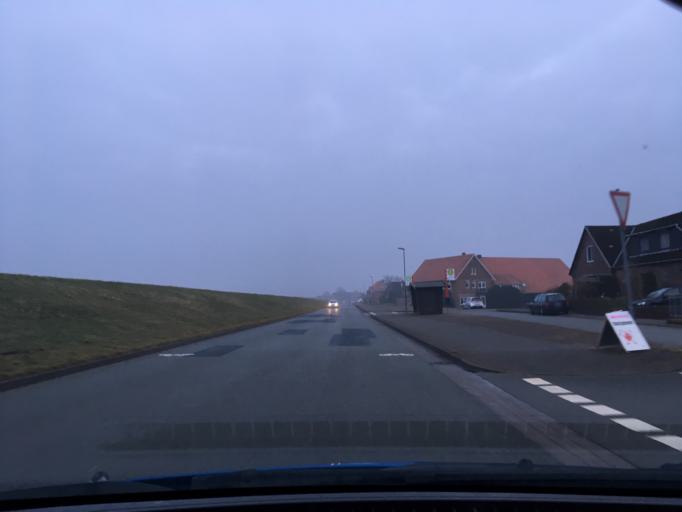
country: DE
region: Lower Saxony
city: Stelle
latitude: 53.4025
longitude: 10.1549
